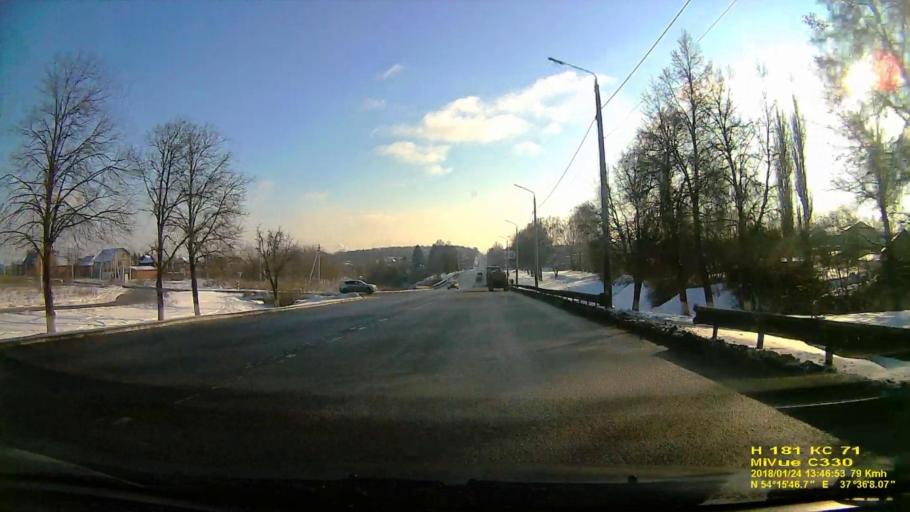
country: RU
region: Tula
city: Gorelki
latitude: 54.2628
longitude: 37.6023
